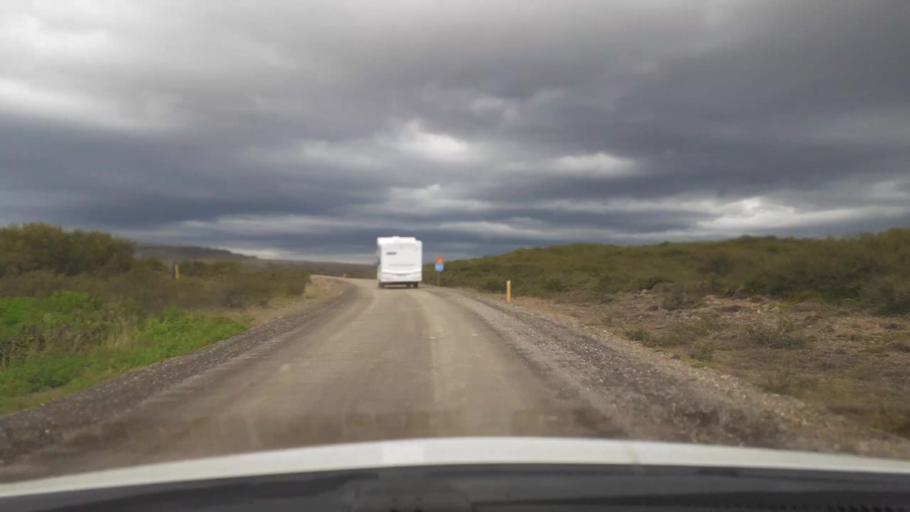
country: IS
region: West
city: Borgarnes
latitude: 64.5512
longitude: -21.6212
